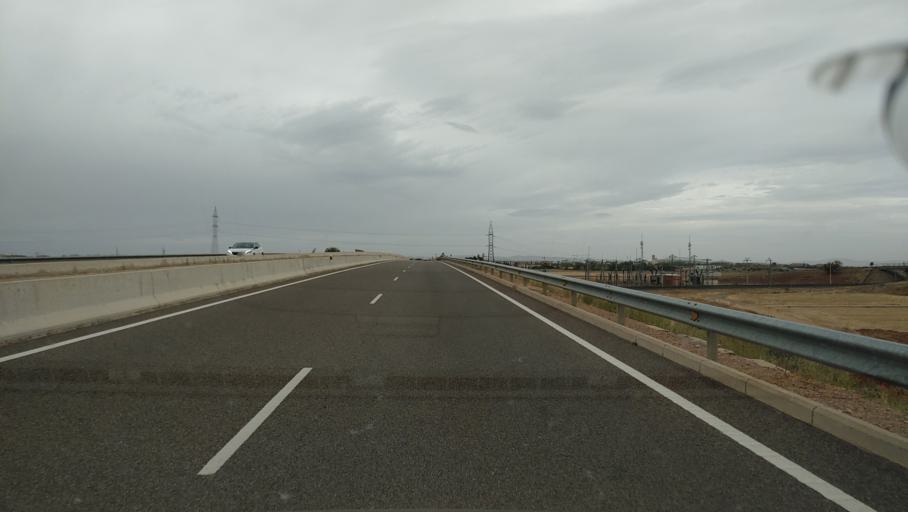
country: ES
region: Castille-La Mancha
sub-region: Provincia de Ciudad Real
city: Miguelturra
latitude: 38.9534
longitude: -3.9189
